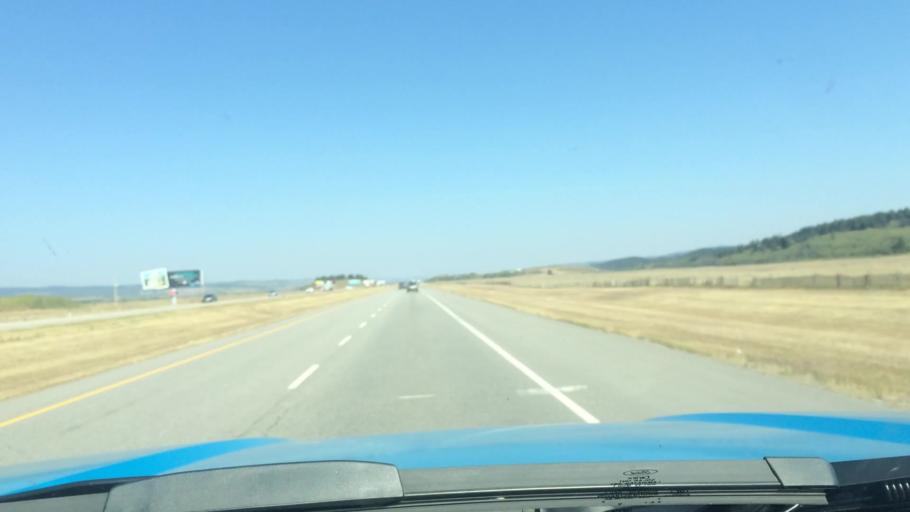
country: CA
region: Alberta
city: Canmore
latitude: 51.1167
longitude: -114.9876
